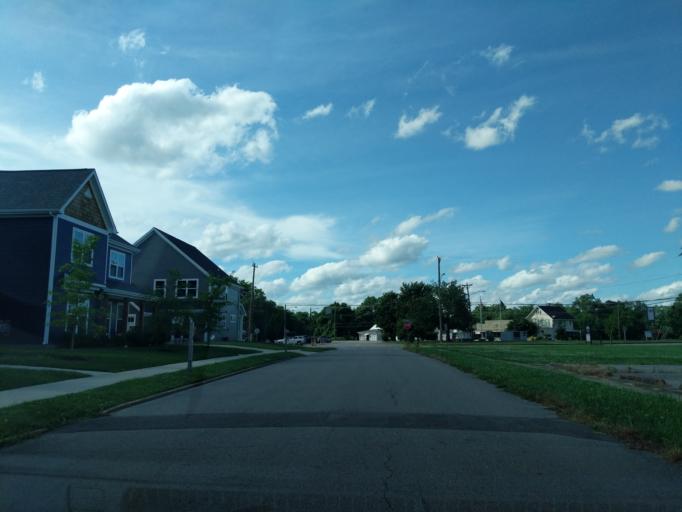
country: US
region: Tennessee
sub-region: Davidson County
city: Lakewood
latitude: 36.2634
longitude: -86.6508
